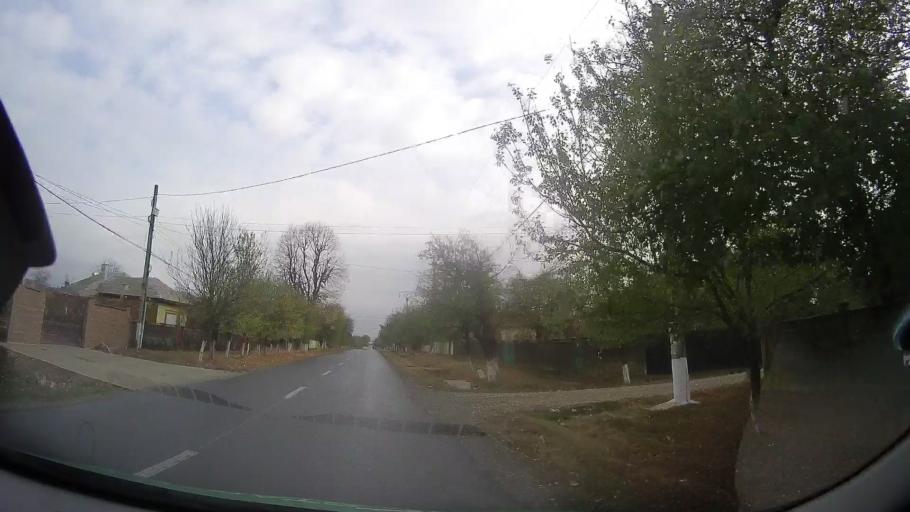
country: RO
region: Ialomita
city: Brazii
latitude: 44.7601
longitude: 26.3635
